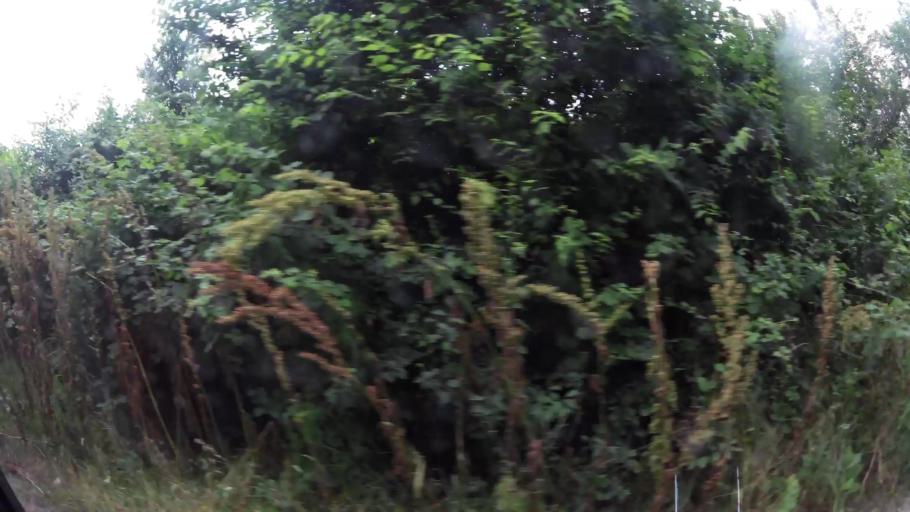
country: GR
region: West Macedonia
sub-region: Nomos Kozanis
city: Kozani
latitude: 40.2981
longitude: 21.8040
